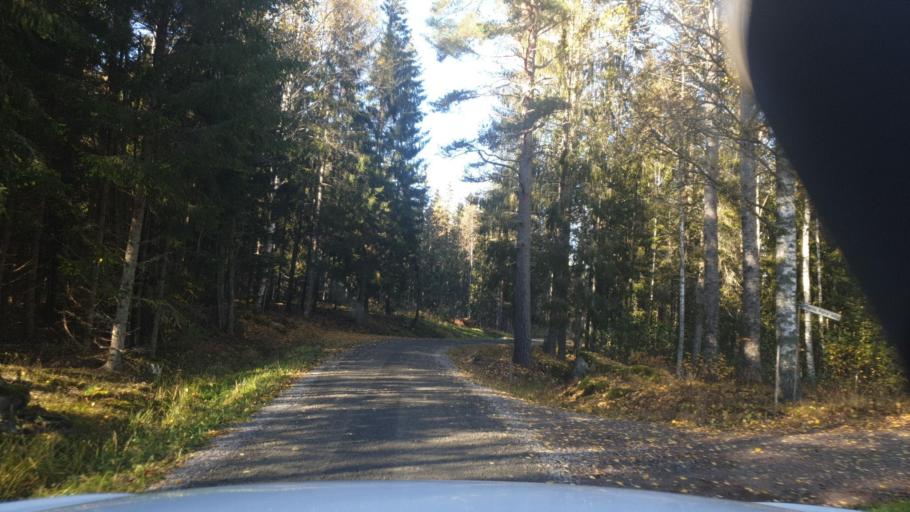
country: SE
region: Vaermland
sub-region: Arvika Kommun
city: Arvika
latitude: 59.5666
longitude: 12.8351
